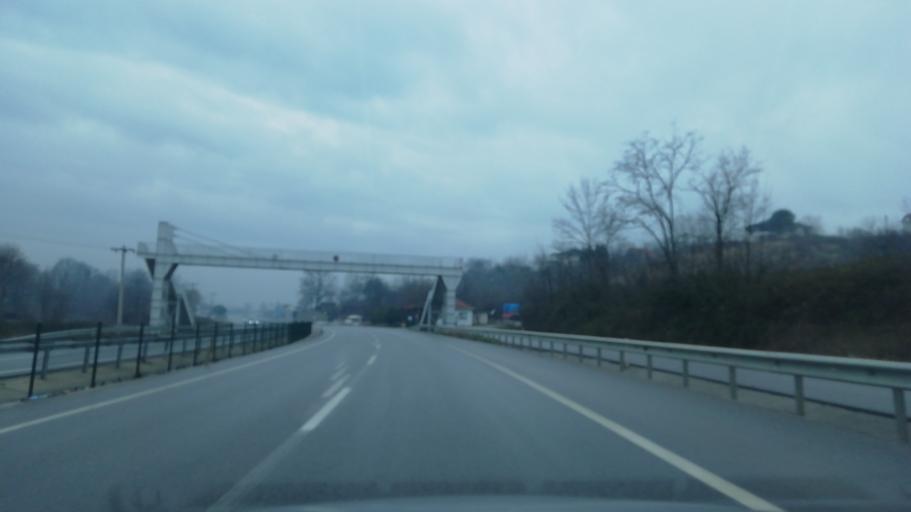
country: TR
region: Sakarya
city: Akyazi
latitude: 40.6299
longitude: 30.6410
